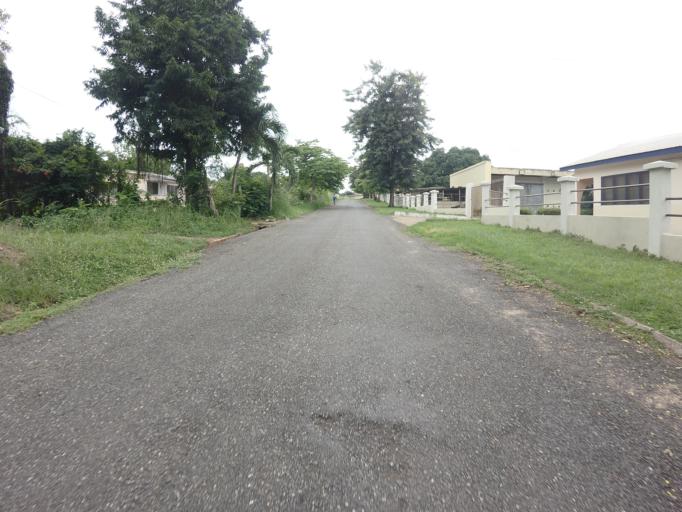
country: GH
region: Volta
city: Ho
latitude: 6.5903
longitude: 0.4670
